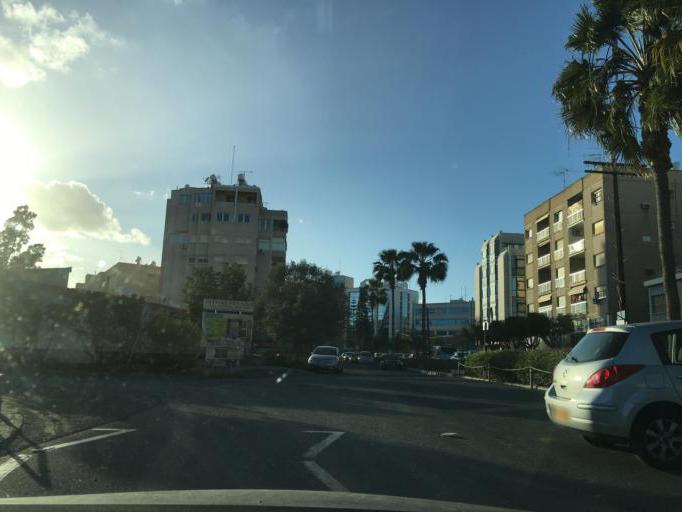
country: CY
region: Limassol
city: Limassol
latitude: 34.6858
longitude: 33.0518
